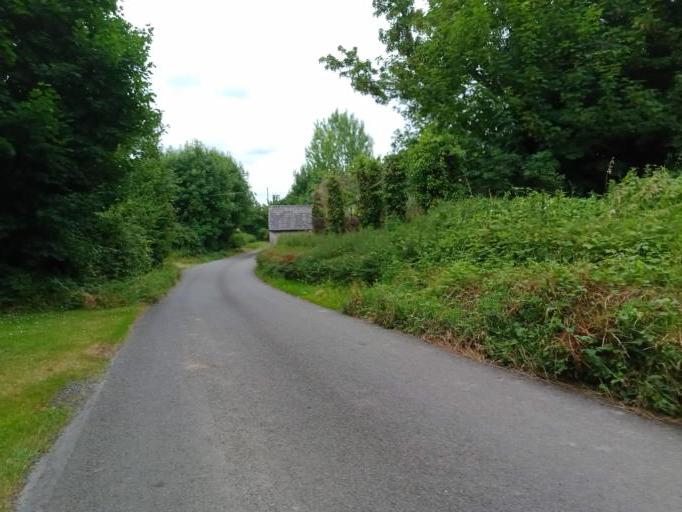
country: IE
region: Leinster
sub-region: Kilkenny
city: Callan
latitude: 52.5342
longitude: -7.3996
